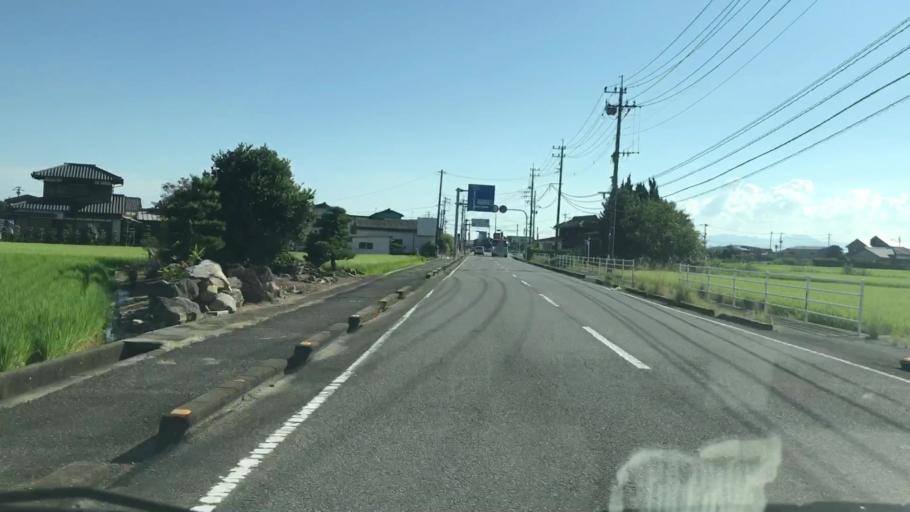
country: JP
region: Saga Prefecture
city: Okawa
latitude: 33.1923
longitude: 130.3327
